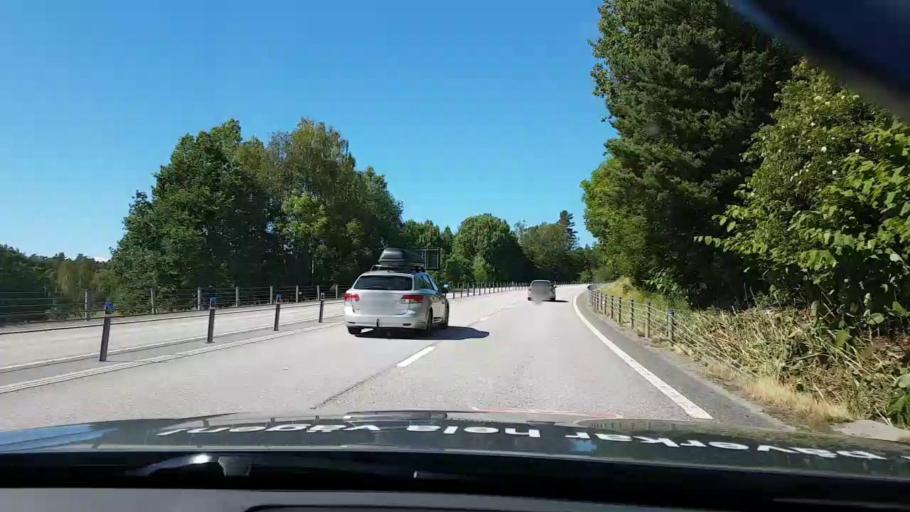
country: SE
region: Kalmar
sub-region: Vasterviks Kommun
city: Gamleby
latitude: 57.8529
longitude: 16.4301
